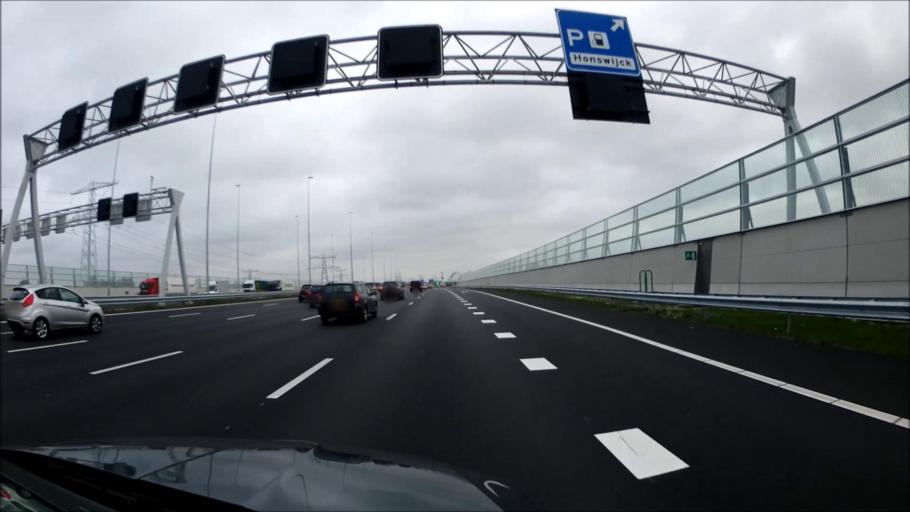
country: NL
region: North Holland
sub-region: Gemeente Weesp
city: Weesp
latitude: 52.3222
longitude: 5.0703
